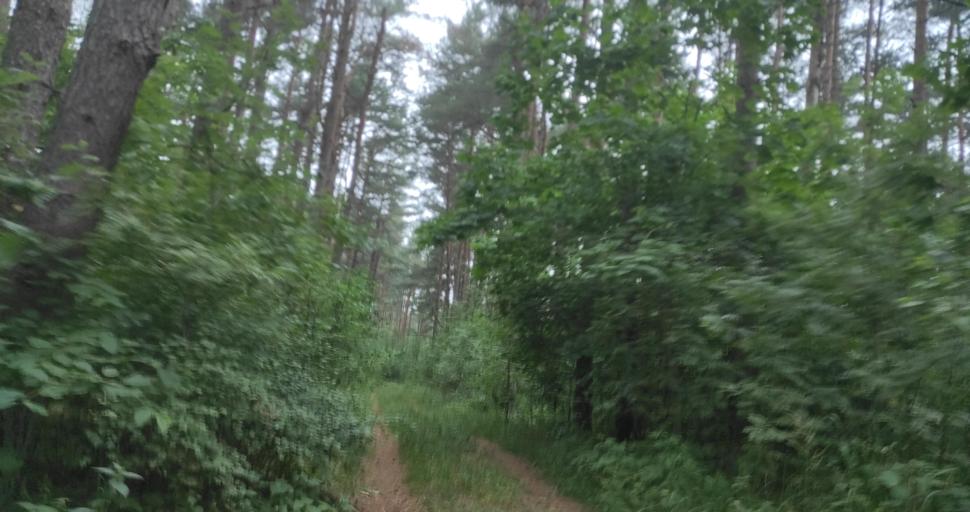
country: LV
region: Pavilostas
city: Pavilosta
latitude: 56.8866
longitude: 21.1985
